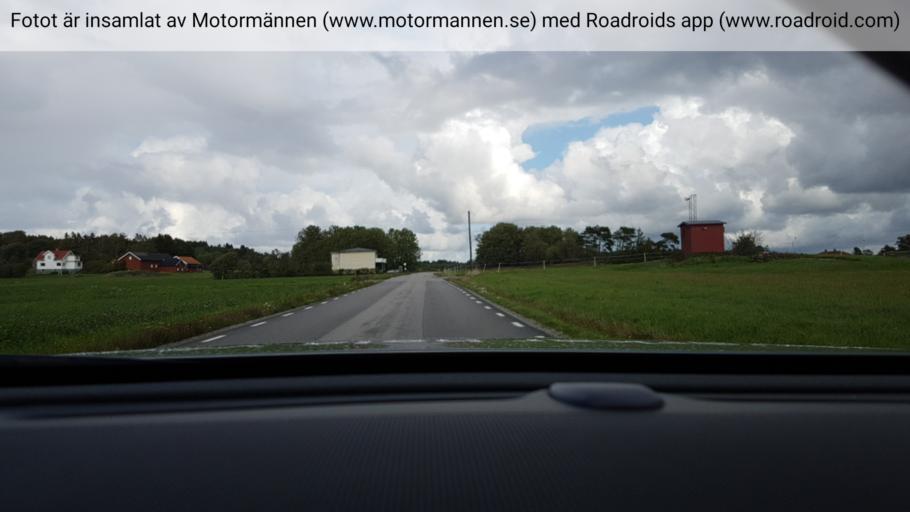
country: SE
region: Vaestra Goetaland
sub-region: Orust
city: Henan
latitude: 58.1532
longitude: 11.5919
